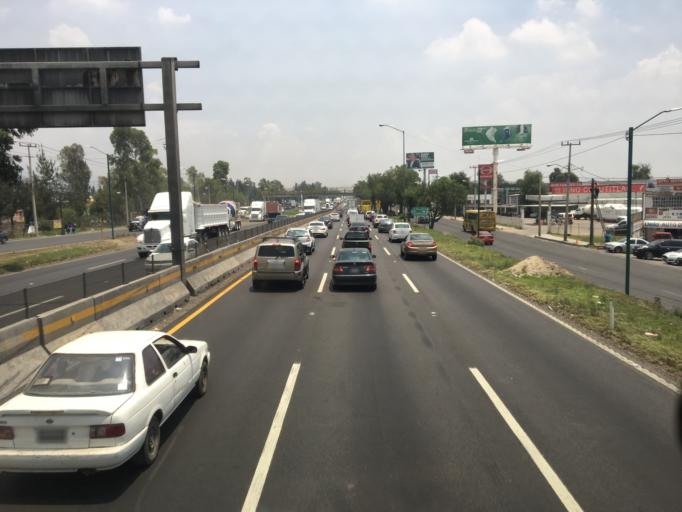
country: MX
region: Mexico
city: Cuautitlan
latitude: 19.6715
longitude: -99.2001
